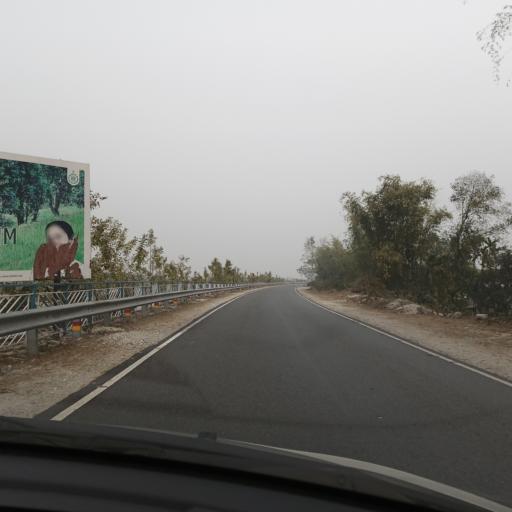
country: IN
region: West Bengal
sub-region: Jalpaiguri
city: Odlabari
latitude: 26.7361
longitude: 88.5752
